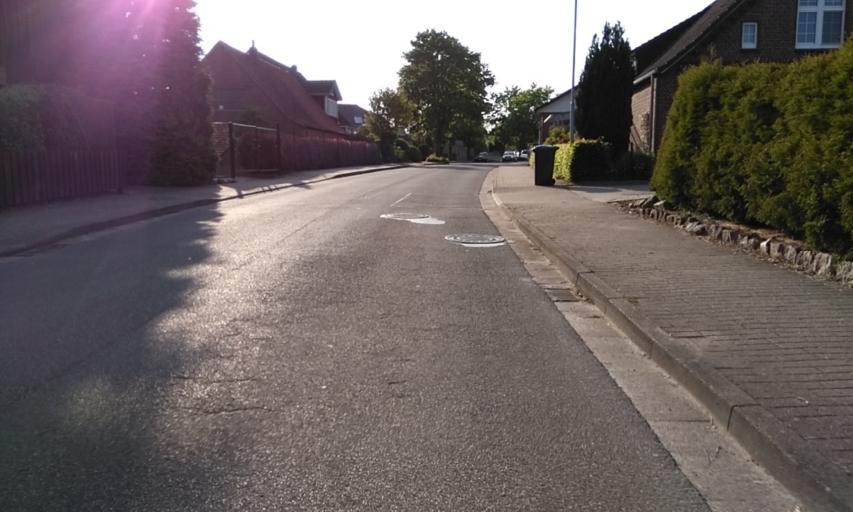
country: DE
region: Lower Saxony
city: Horneburg
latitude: 53.5040
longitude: 9.5744
